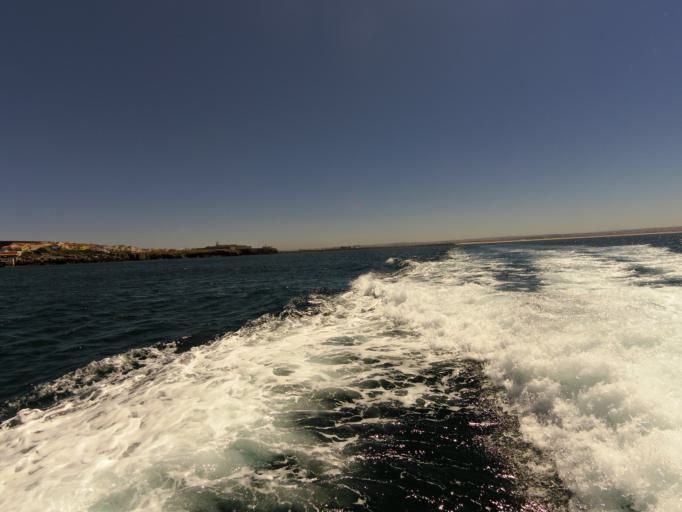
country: PT
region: Leiria
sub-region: Peniche
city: Peniche
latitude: 39.3501
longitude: -9.3900
